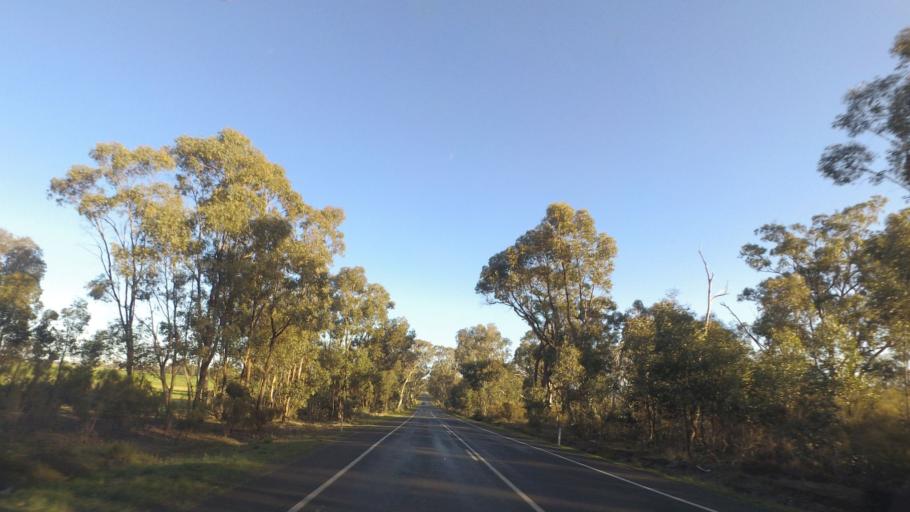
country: AU
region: Victoria
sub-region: Mount Alexander
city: Castlemaine
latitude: -37.0793
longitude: 144.5079
